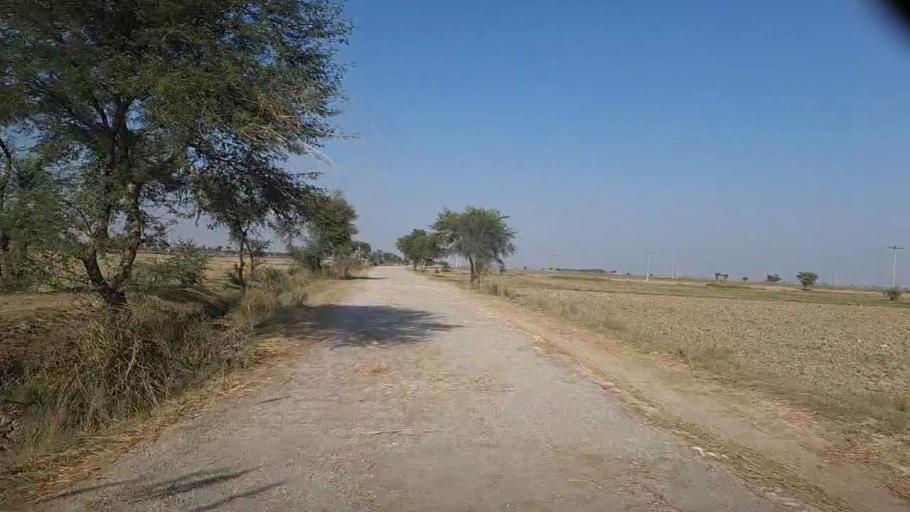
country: PK
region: Sindh
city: Thul
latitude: 28.3580
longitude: 68.7659
